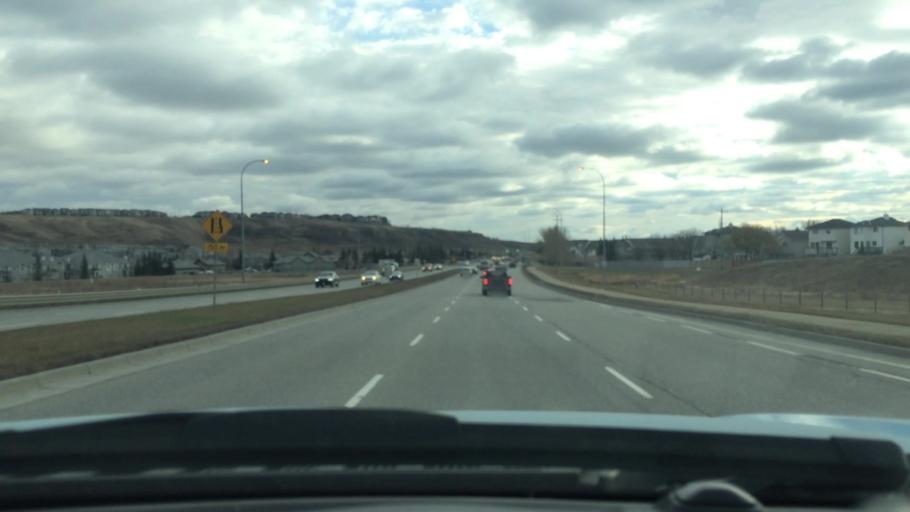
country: CA
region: Alberta
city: Calgary
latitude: 51.1552
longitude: -114.1112
